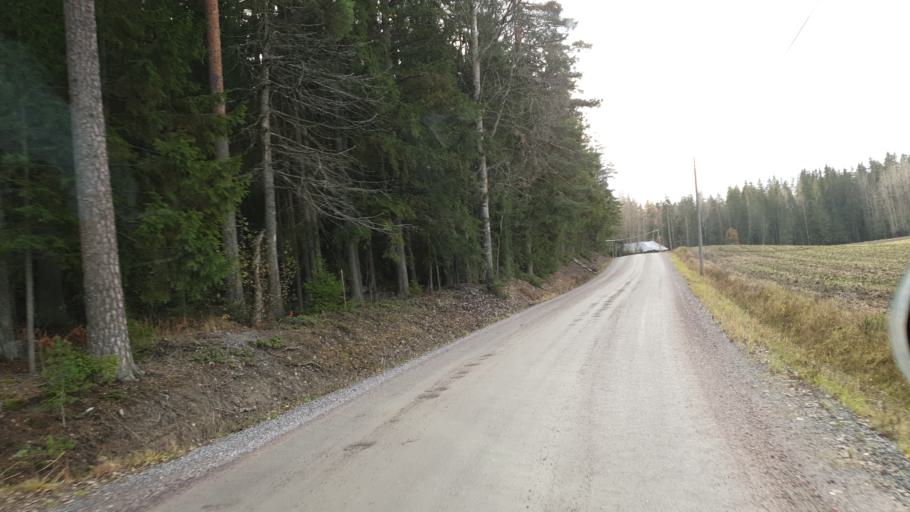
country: FI
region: Uusimaa
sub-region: Helsinki
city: Siuntio
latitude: 60.2438
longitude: 24.3034
